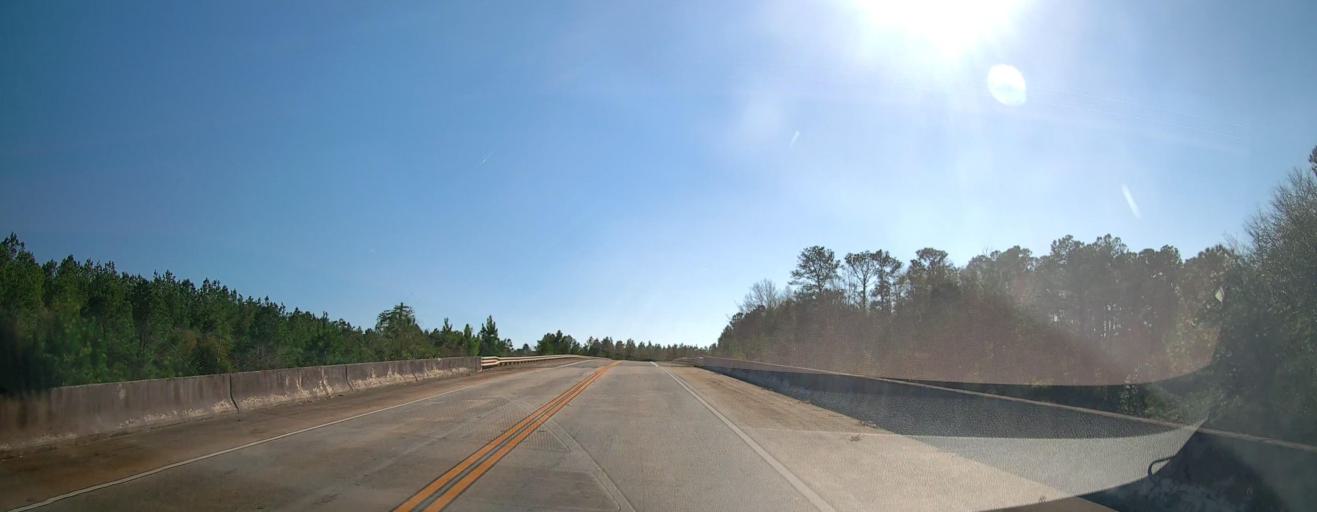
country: US
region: Georgia
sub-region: Macon County
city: Oglethorpe
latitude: 32.2217
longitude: -84.1013
